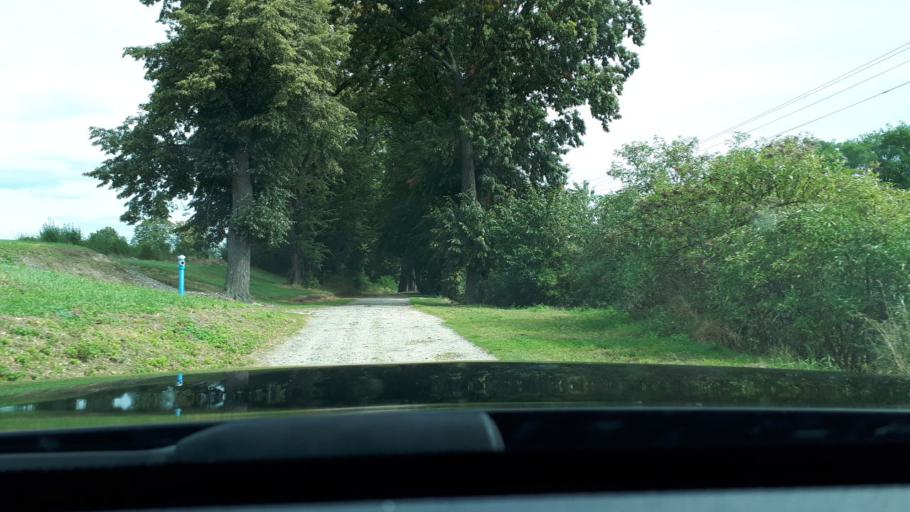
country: PL
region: Lower Silesian Voivodeship
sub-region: Powiat zlotoryjski
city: Olszanica
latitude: 51.2389
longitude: 15.8177
